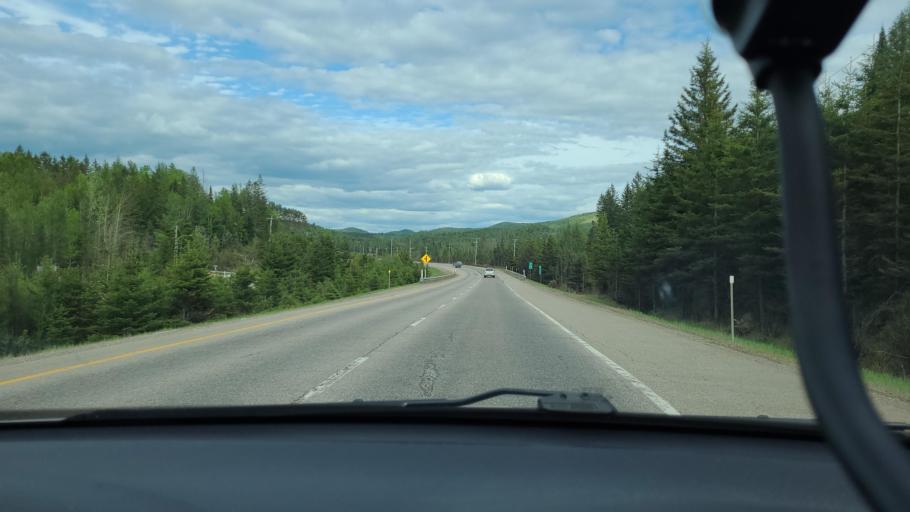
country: CA
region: Quebec
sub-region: Laurentides
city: Mont-Tremblant
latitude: 46.1121
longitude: -74.5325
